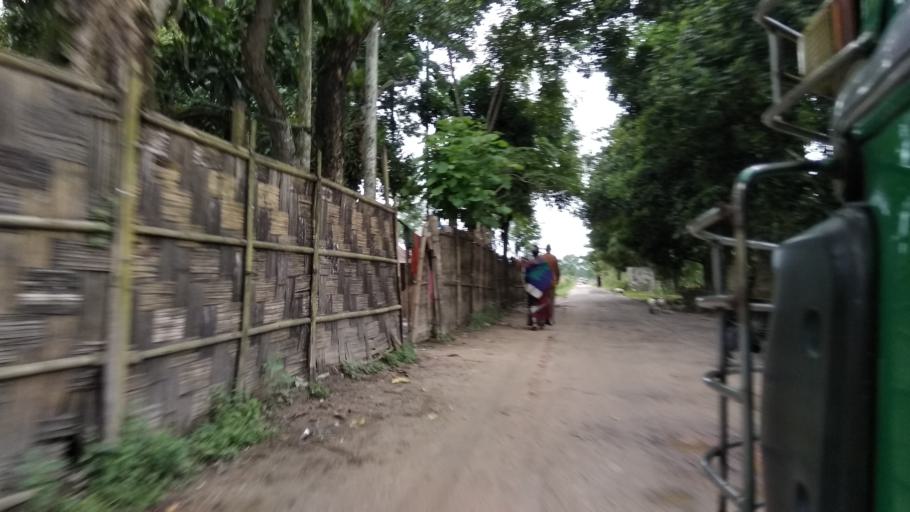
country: IN
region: Tripura
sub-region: Dhalai
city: Kamalpur
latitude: 24.2091
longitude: 91.8625
